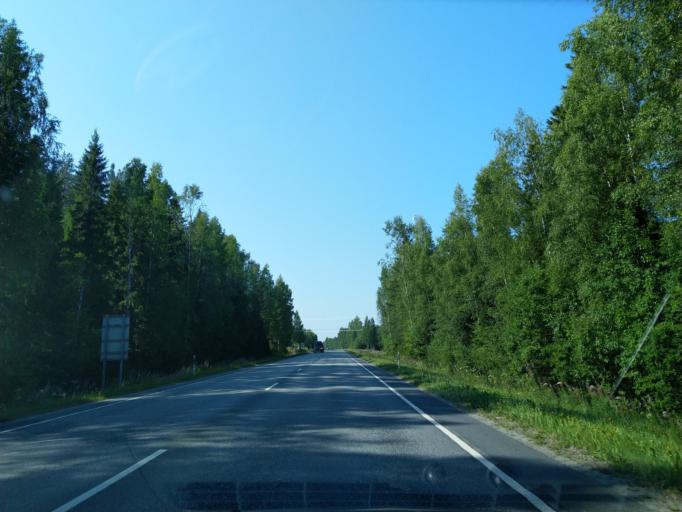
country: FI
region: Satakunta
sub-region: Pori
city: Pomarkku
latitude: 61.6875
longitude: 21.9959
